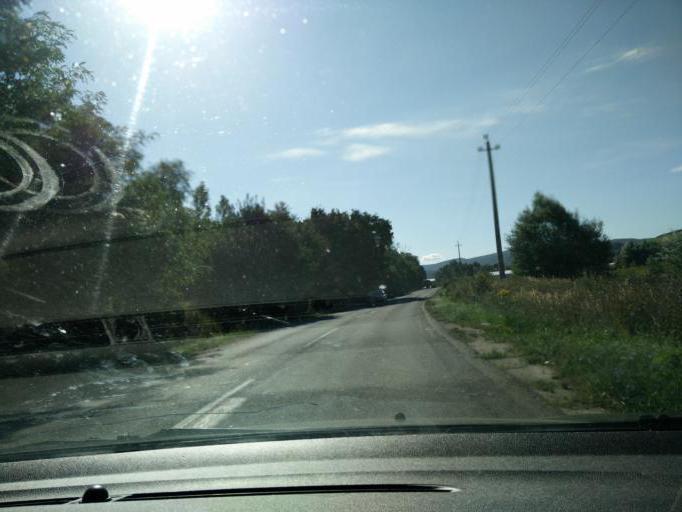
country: HU
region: Pest
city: Piliscsaba
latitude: 47.6406
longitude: 18.8128
